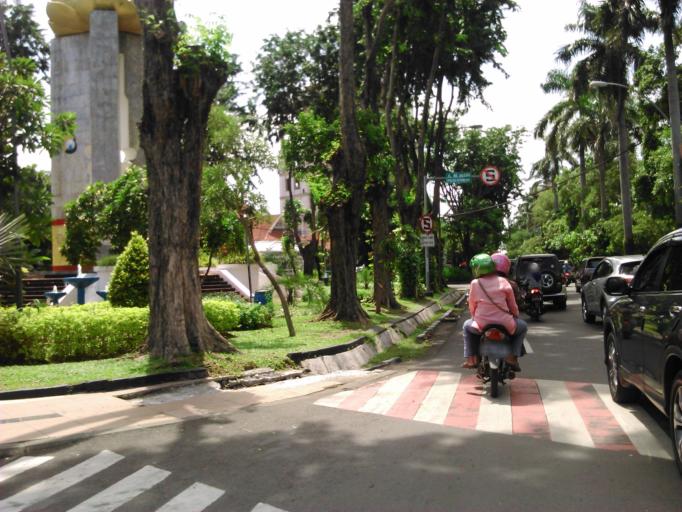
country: ID
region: East Java
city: Gubengairlangga
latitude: -7.2812
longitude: 112.7407
